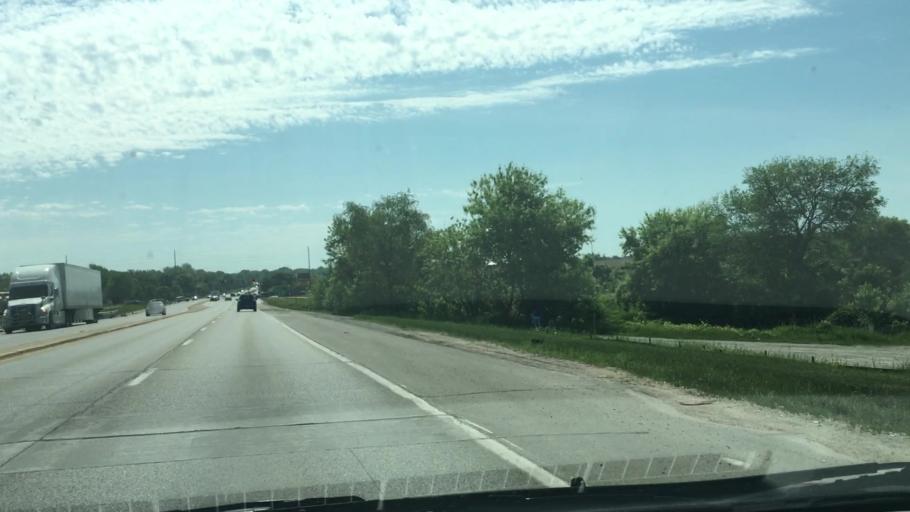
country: US
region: Iowa
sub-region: Johnson County
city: Iowa City
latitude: 41.6463
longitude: -91.5356
